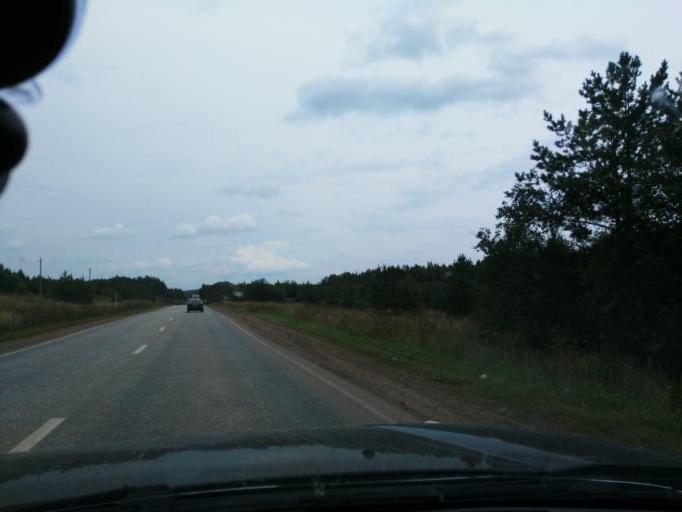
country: RU
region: Perm
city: Kuyeda
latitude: 56.4786
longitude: 55.7730
